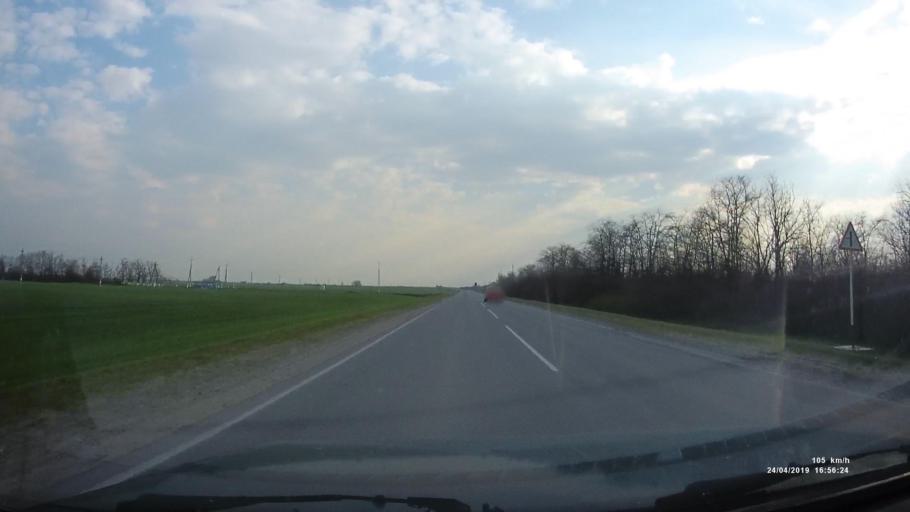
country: RU
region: Rostov
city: Proletarsk
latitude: 46.6522
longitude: 41.6787
